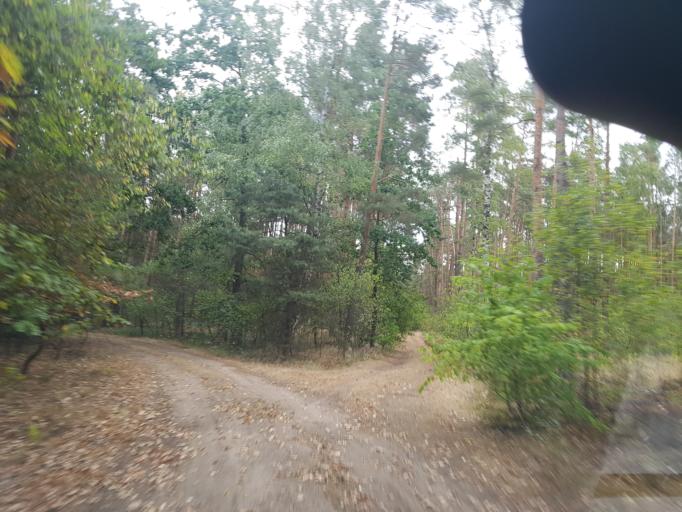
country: DE
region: Brandenburg
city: Schilda
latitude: 51.5644
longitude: 13.3285
